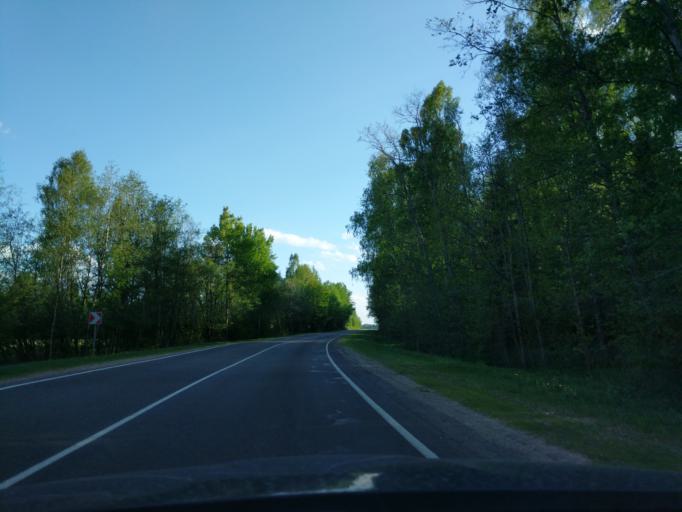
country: BY
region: Minsk
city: Kryvichy
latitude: 54.6522
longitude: 27.1749
